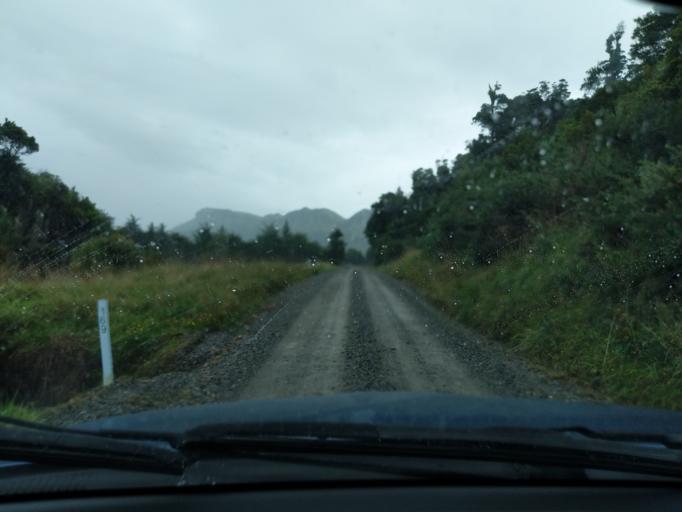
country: NZ
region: Tasman
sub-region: Tasman District
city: Takaka
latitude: -40.6509
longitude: 172.4664
